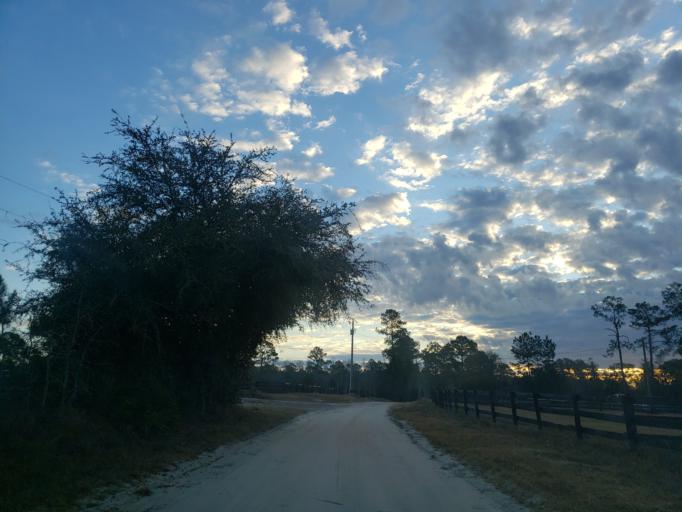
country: US
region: Georgia
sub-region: Chatham County
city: Bloomingdale
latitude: 32.1143
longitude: -81.3480
